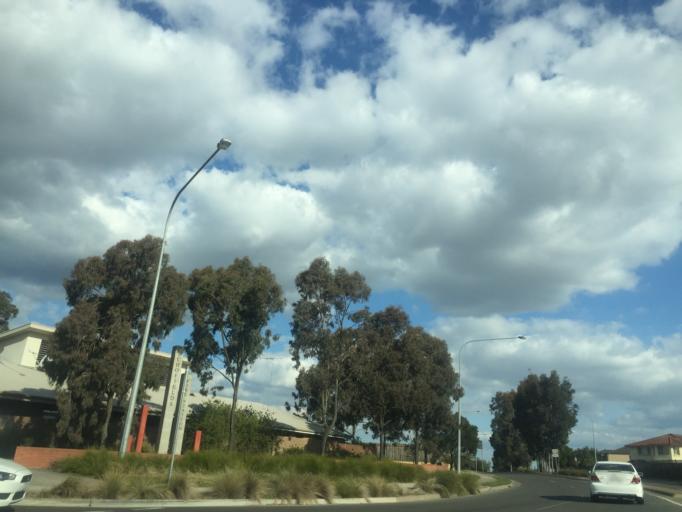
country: AU
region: New South Wales
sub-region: Blacktown
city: Quakers Hill
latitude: -33.7129
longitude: 150.8934
